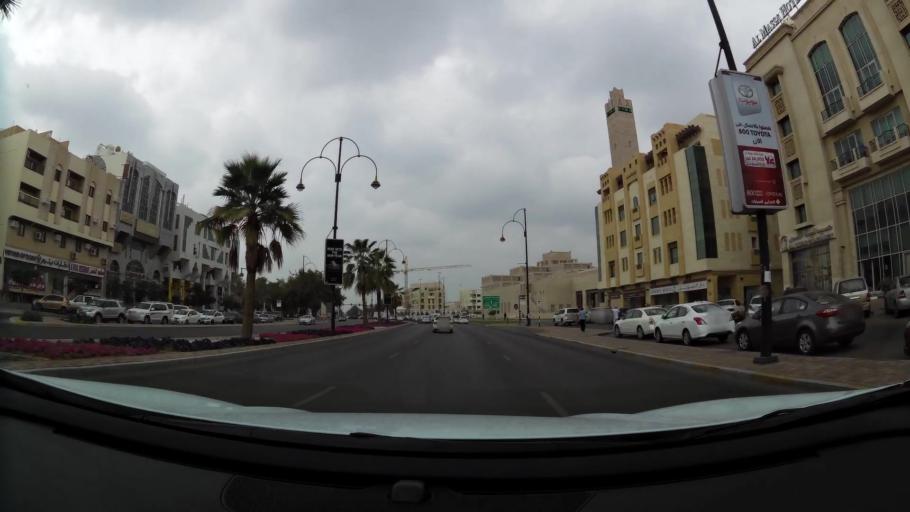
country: AE
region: Abu Dhabi
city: Al Ain
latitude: 24.2224
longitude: 55.7680
